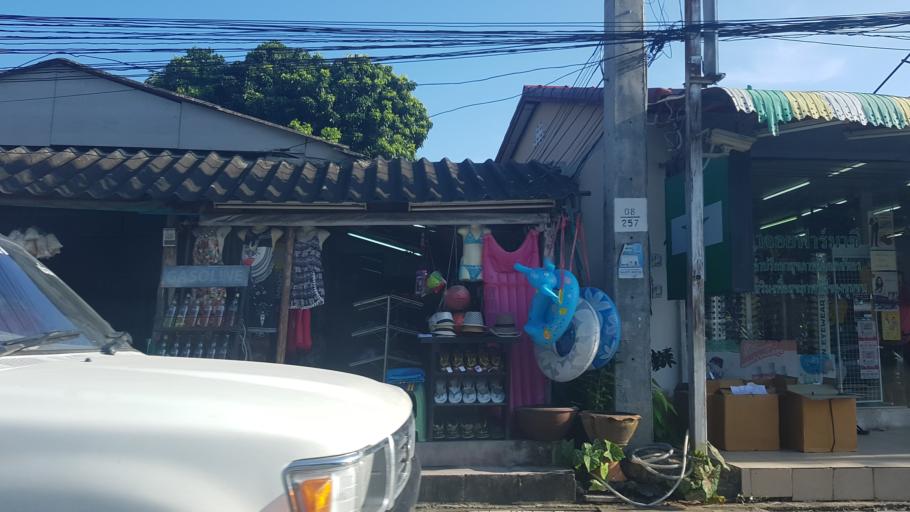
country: TH
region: Surat Thani
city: Ko Samui
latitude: 9.5591
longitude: 100.0583
